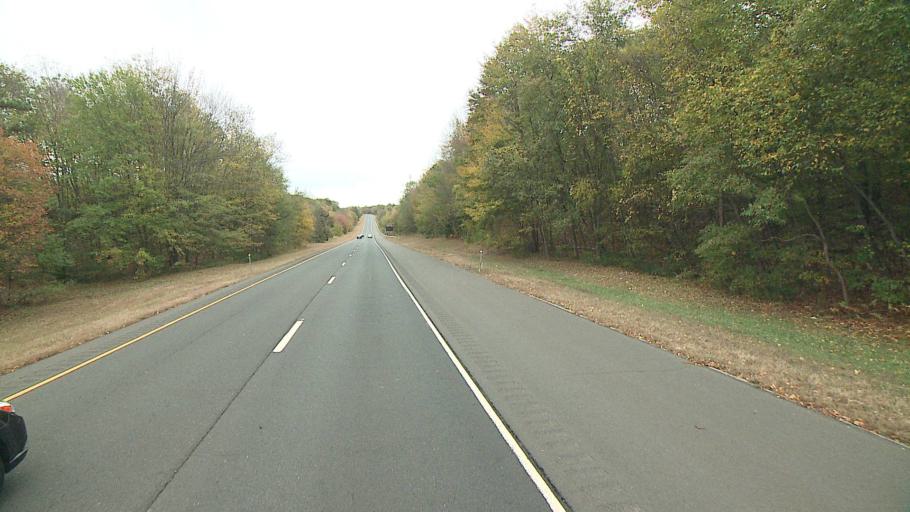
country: US
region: Connecticut
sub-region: Middlesex County
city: East Haddam
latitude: 41.4424
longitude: -72.5190
